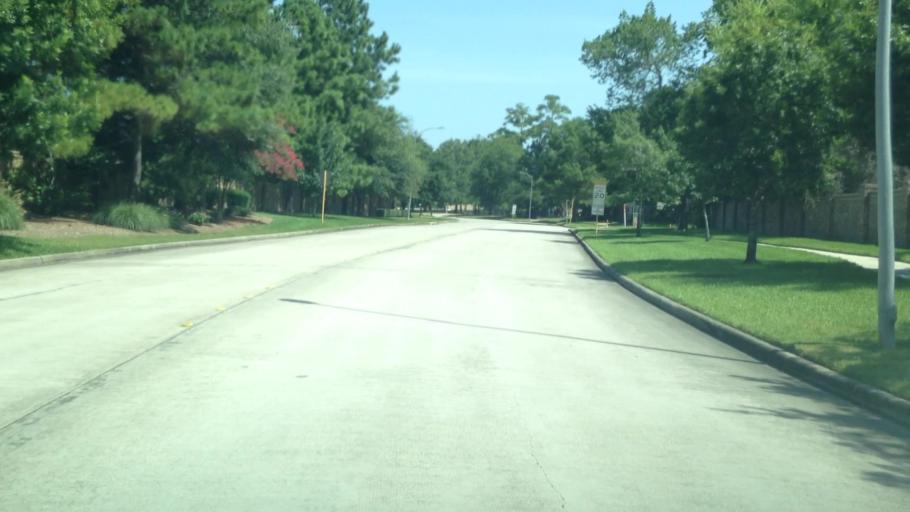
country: US
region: Texas
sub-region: Harris County
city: Sheldon
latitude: 29.9245
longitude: -95.1758
